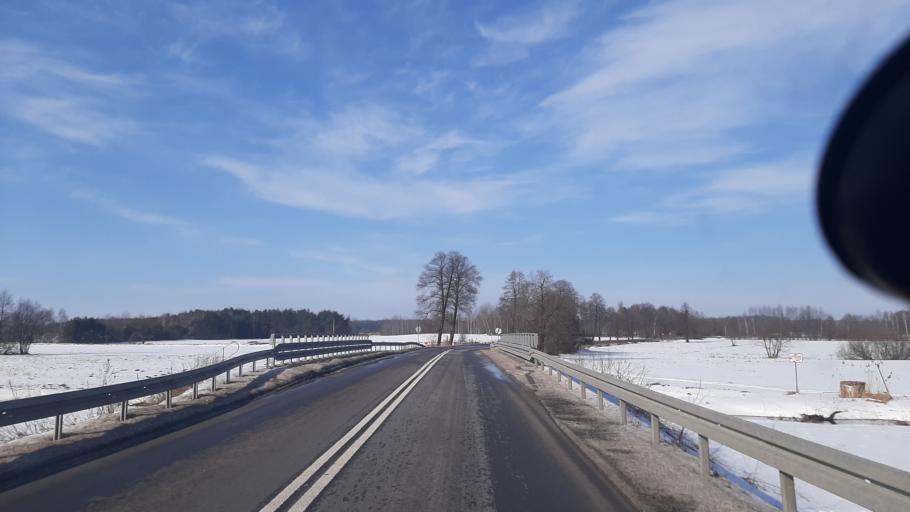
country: PL
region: Lublin Voivodeship
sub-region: Powiat pulawski
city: Kurow
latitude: 51.4121
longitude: 22.2043
